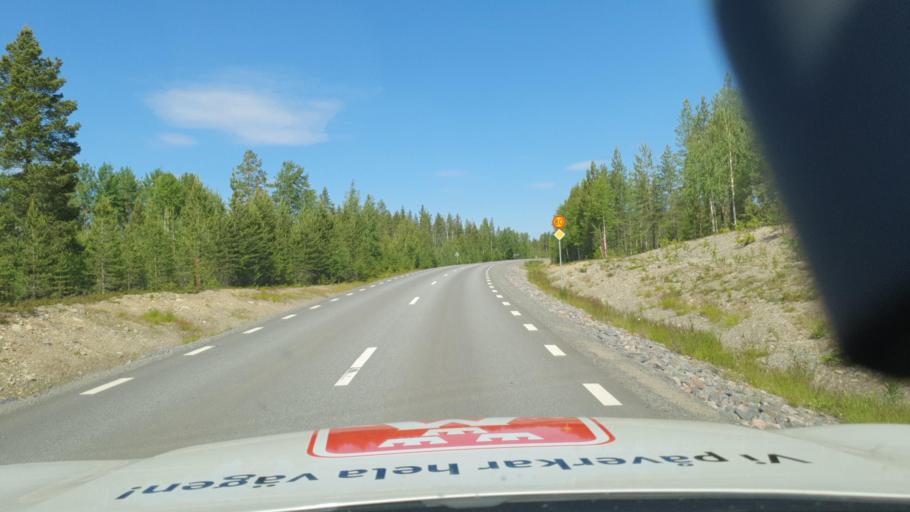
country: SE
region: Vaesterbotten
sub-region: Skelleftea Kommun
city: Langsele
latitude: 64.7544
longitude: 20.3403
